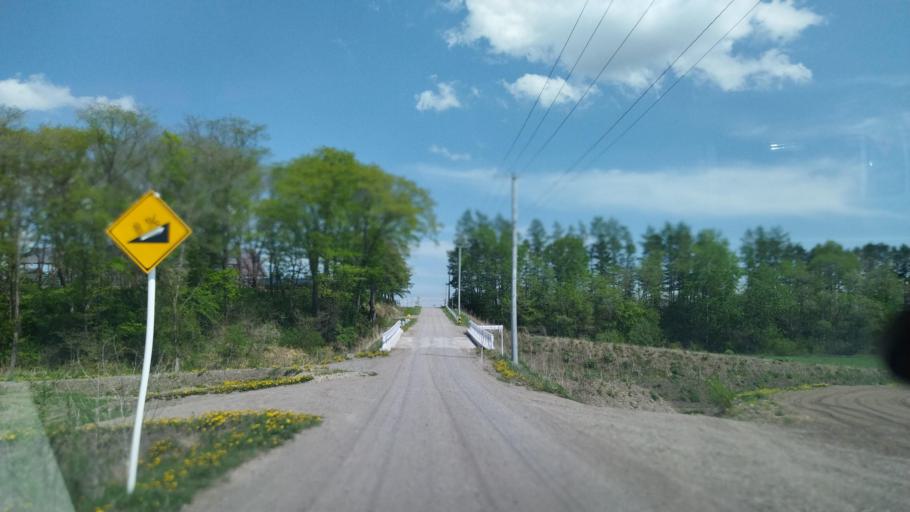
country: JP
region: Hokkaido
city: Otofuke
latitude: 43.1317
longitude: 143.2214
